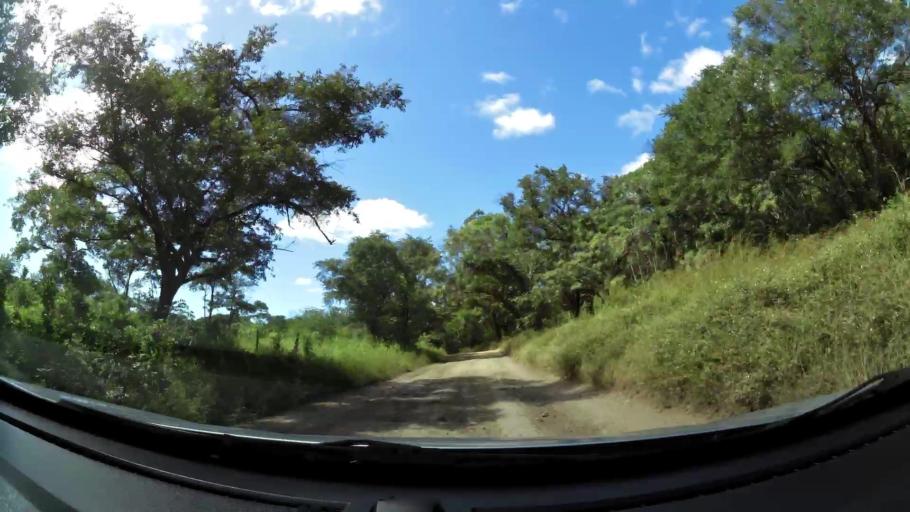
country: CR
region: Guanacaste
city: Bagaces
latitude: 10.5300
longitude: -85.2905
